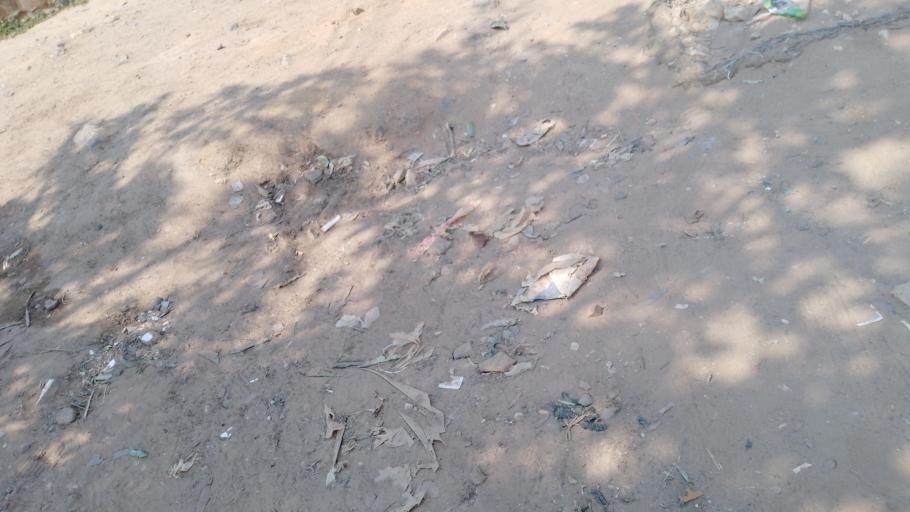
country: ZM
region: Lusaka
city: Lusaka
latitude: -15.3972
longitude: 28.3672
